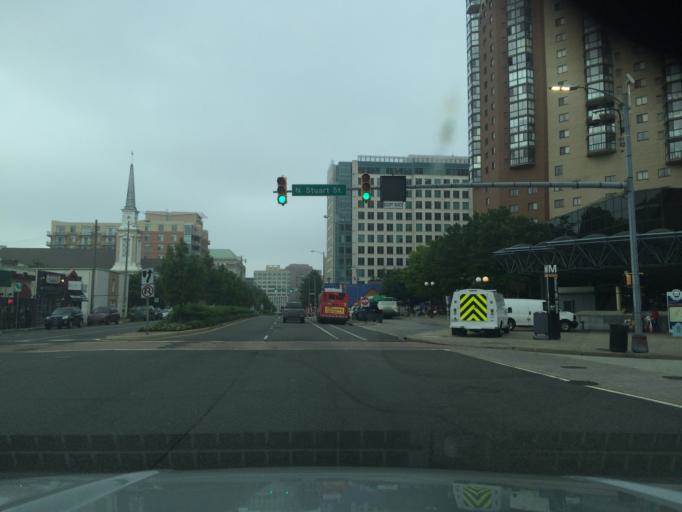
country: US
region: Virginia
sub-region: Arlington County
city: Arlington
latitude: 38.8821
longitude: -77.1120
